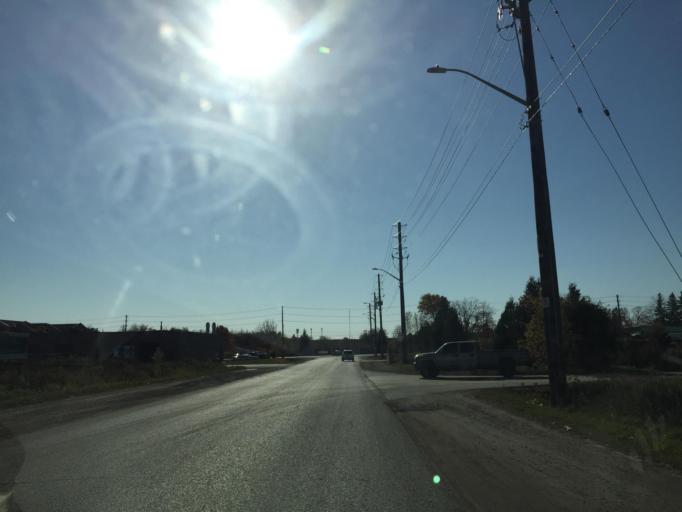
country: CA
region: Ontario
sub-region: Wellington County
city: Guelph
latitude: 43.5543
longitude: -80.2973
